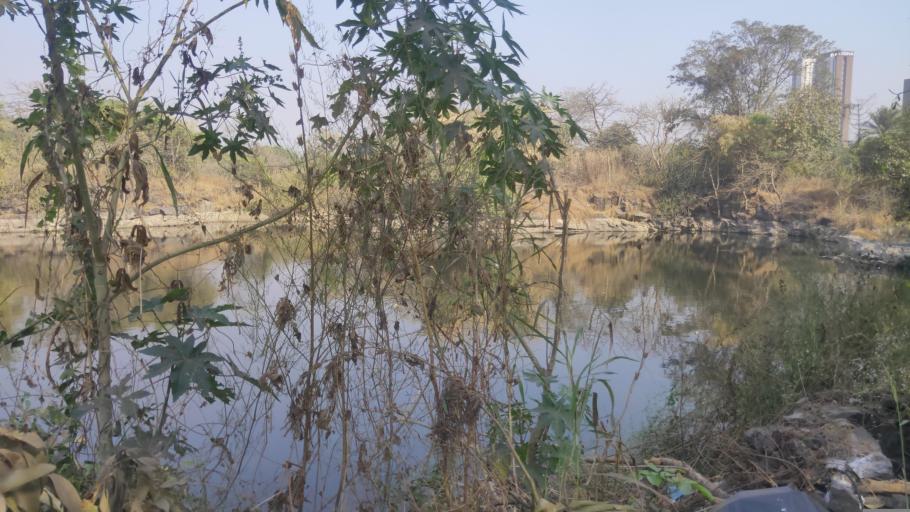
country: IN
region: Maharashtra
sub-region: Thane
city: Dombivli
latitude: 19.2365
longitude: 73.0429
